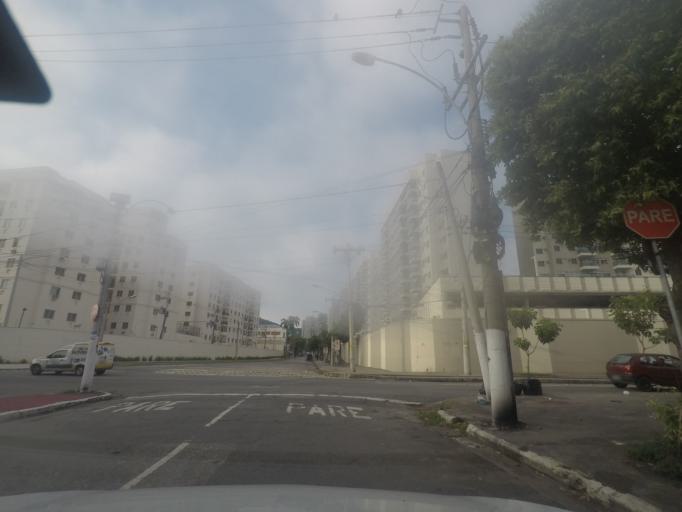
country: BR
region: Rio de Janeiro
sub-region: Duque De Caxias
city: Duque de Caxias
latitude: -22.8369
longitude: -43.2742
